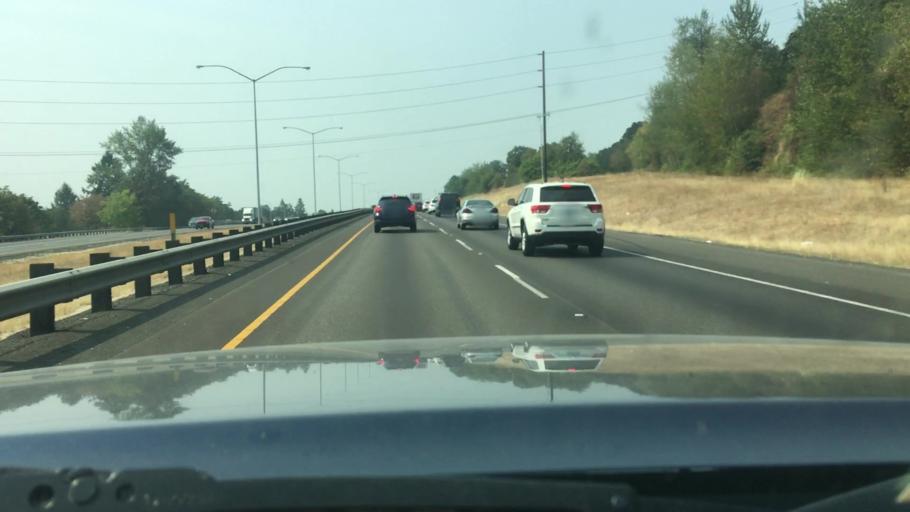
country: US
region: Oregon
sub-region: Clackamas County
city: West Linn
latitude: 45.3542
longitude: -122.6234
